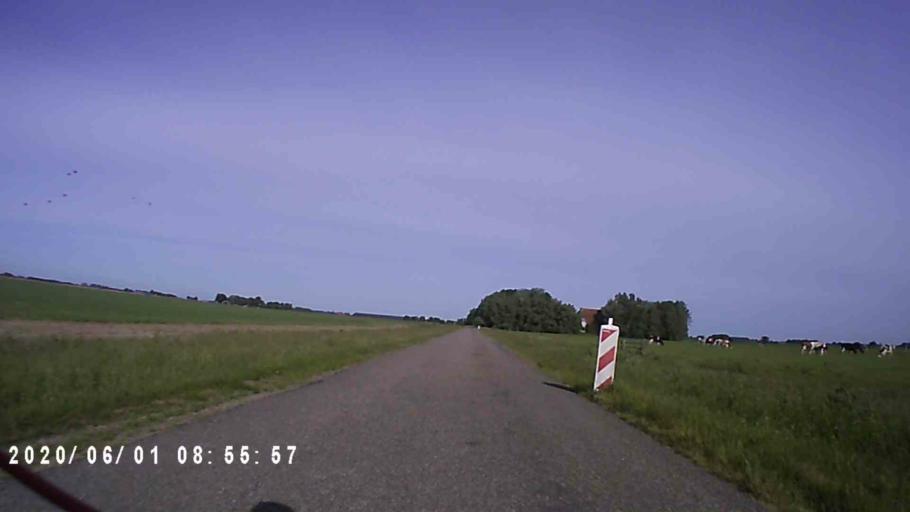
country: NL
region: Friesland
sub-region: Gemeente Leeuwarderadeel
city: Britsum
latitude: 53.2789
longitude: 5.8216
